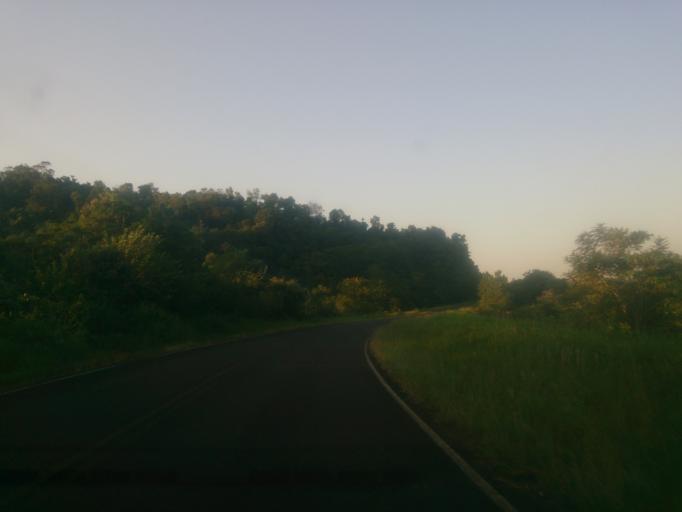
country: AR
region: Misiones
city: Panambi
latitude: -27.6990
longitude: -54.9073
